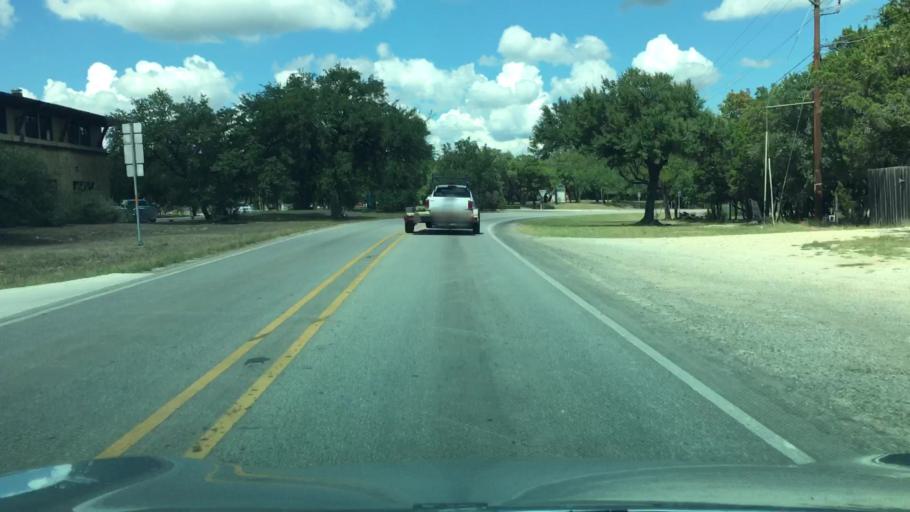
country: US
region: Texas
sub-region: Hays County
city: Wimberley
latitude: 29.9969
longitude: -98.0903
